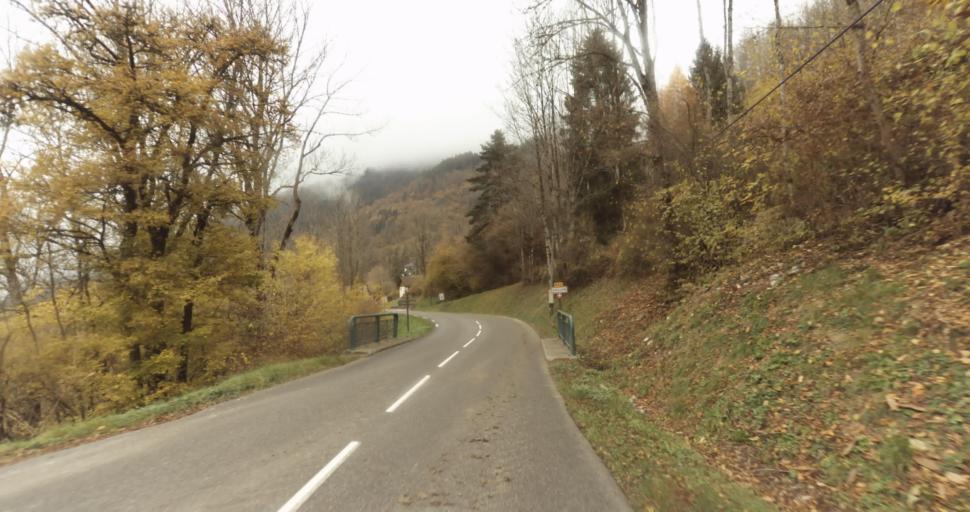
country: FR
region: Rhone-Alpes
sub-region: Departement de la Haute-Savoie
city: Thorens-Glieres
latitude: 45.9826
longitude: 6.2826
